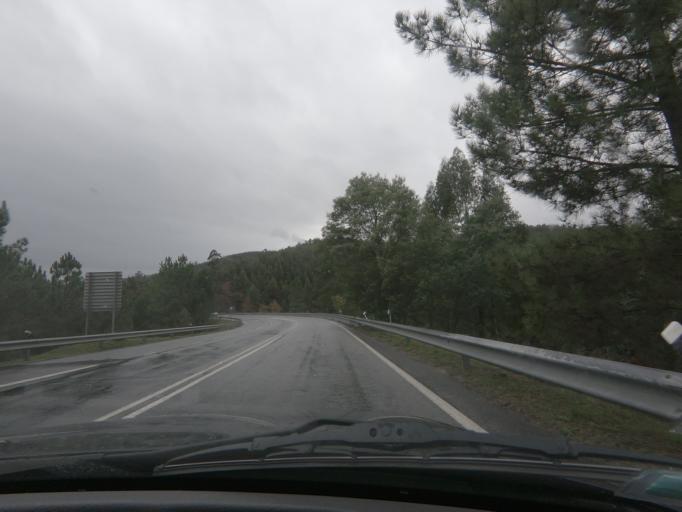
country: PT
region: Braga
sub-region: Celorico de Basto
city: Celorico de Basto
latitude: 41.3382
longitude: -8.0381
